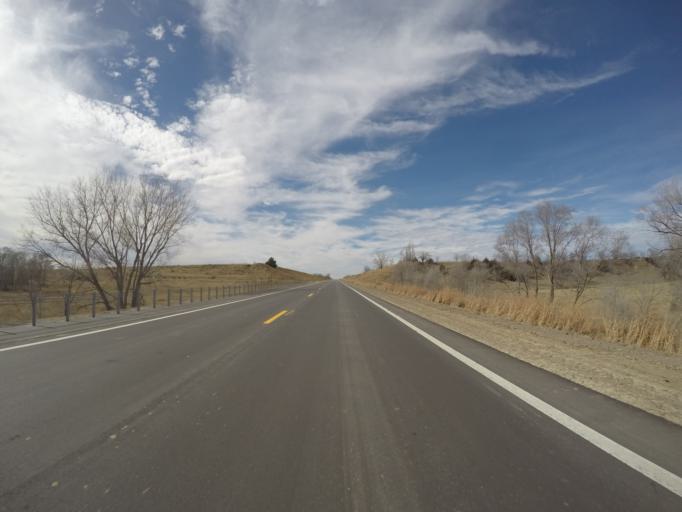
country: US
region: Nebraska
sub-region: Franklin County
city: Franklin
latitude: 40.0962
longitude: -98.9192
